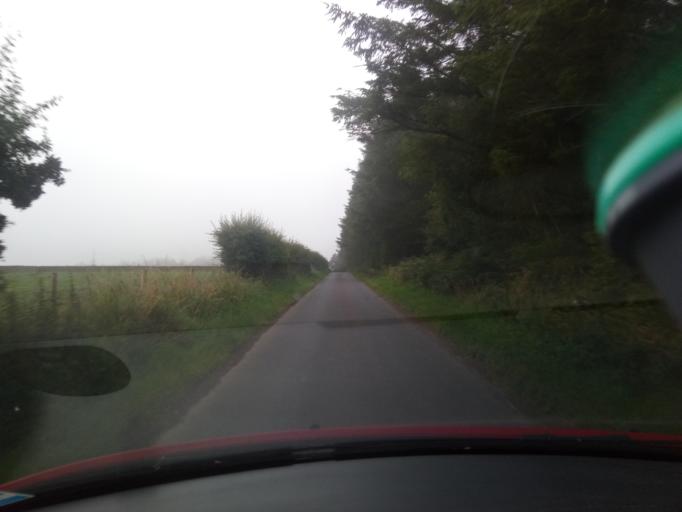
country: GB
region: Scotland
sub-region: The Scottish Borders
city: Melrose
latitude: 55.6494
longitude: -2.7272
